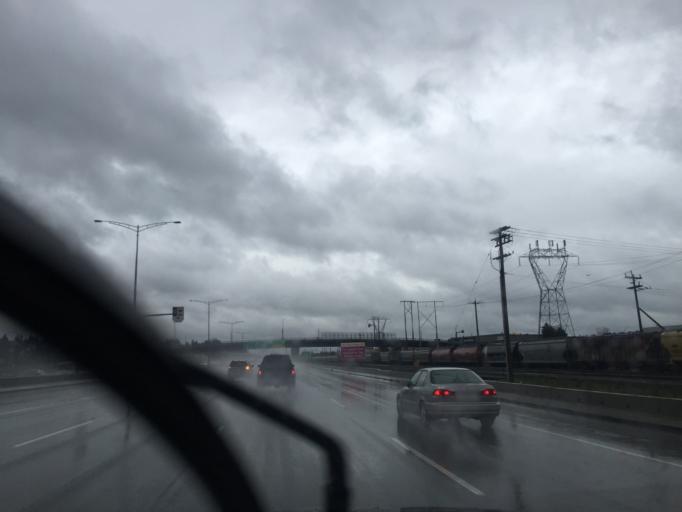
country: CA
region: British Columbia
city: Port Moody
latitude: 49.2326
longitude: -122.8656
